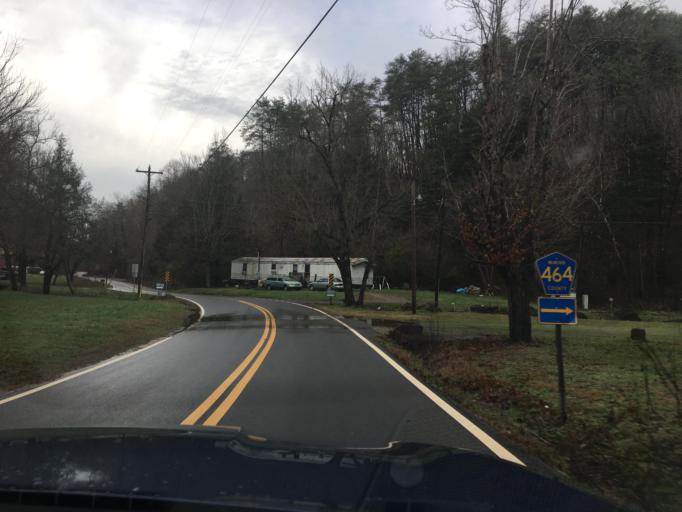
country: US
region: Tennessee
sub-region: McMinn County
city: Englewood
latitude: 35.3981
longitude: -84.4434
